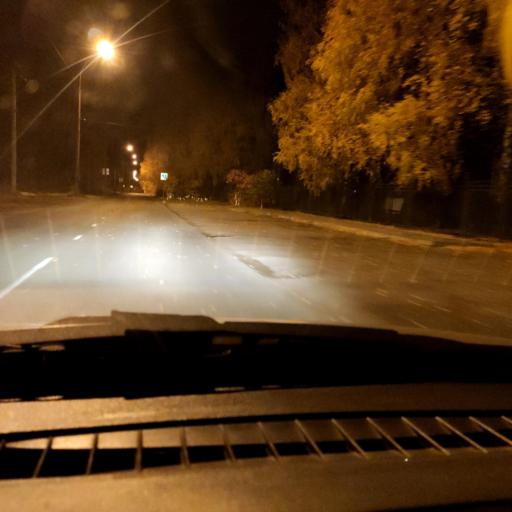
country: RU
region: Samara
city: Tol'yatti
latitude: 53.5056
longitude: 49.3055
